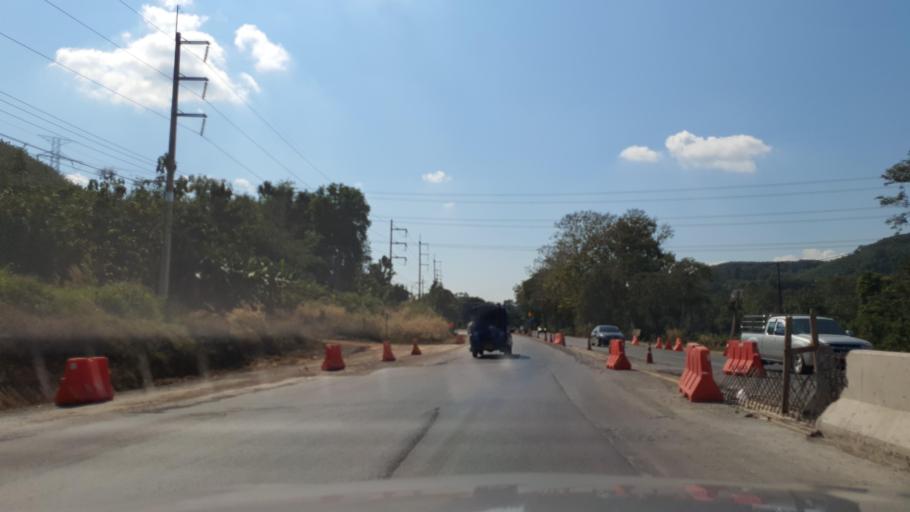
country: TH
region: Nan
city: Nan
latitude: 18.9013
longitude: 100.7578
